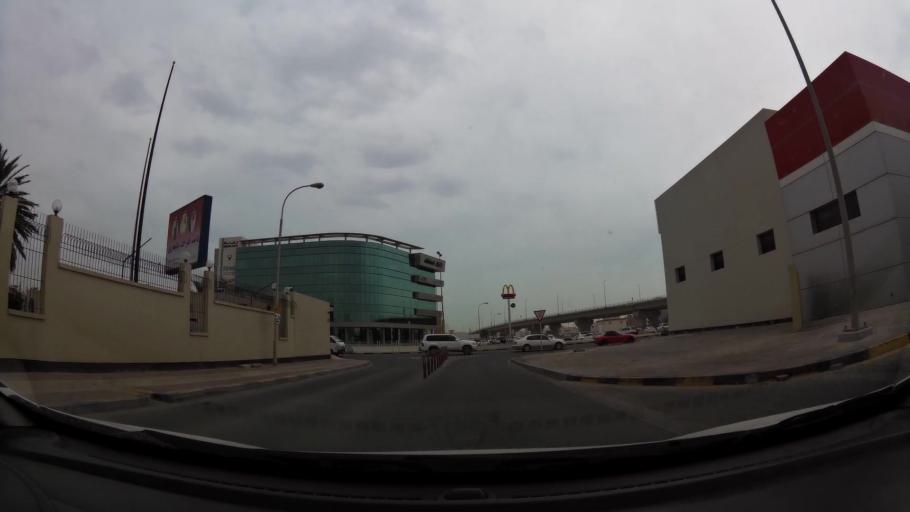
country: BH
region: Northern
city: Madinat `Isa
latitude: 26.1684
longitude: 50.5416
